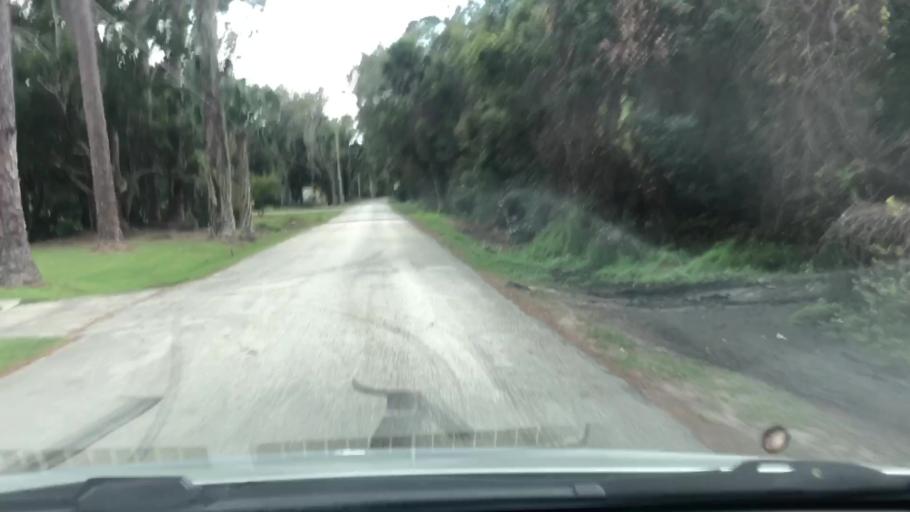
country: US
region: Florida
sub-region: Volusia County
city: Deltona
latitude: 28.8736
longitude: -81.2674
